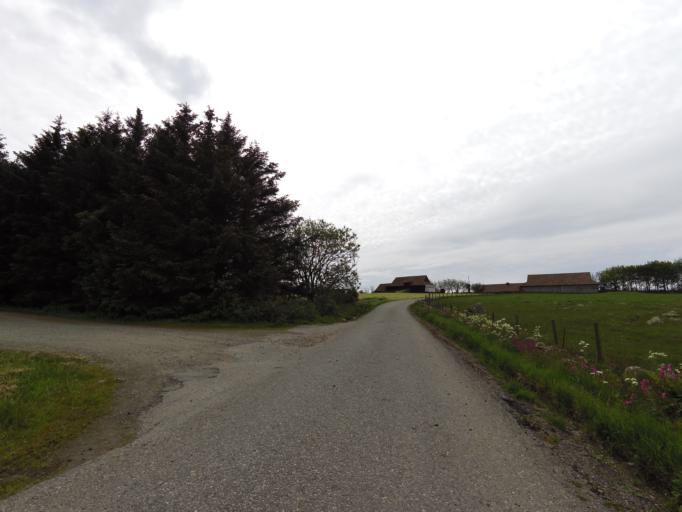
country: NO
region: Rogaland
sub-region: Ha
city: Naerbo
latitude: 58.6367
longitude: 5.6006
